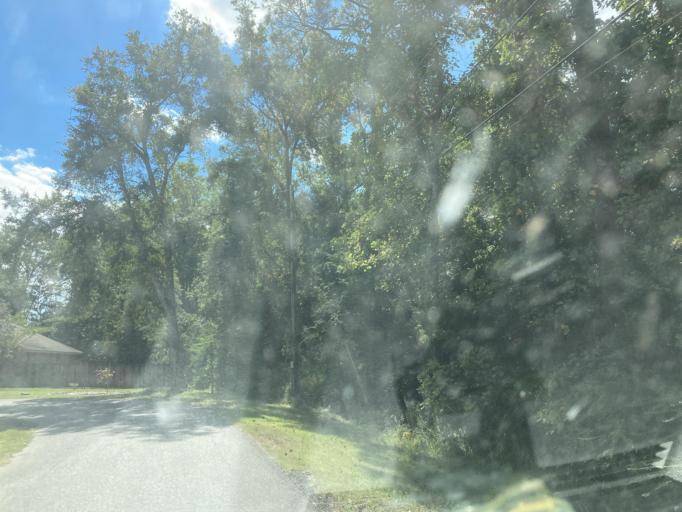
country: US
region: Mississippi
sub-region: Jackson County
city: Gulf Hills
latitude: 30.4461
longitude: -88.8455
